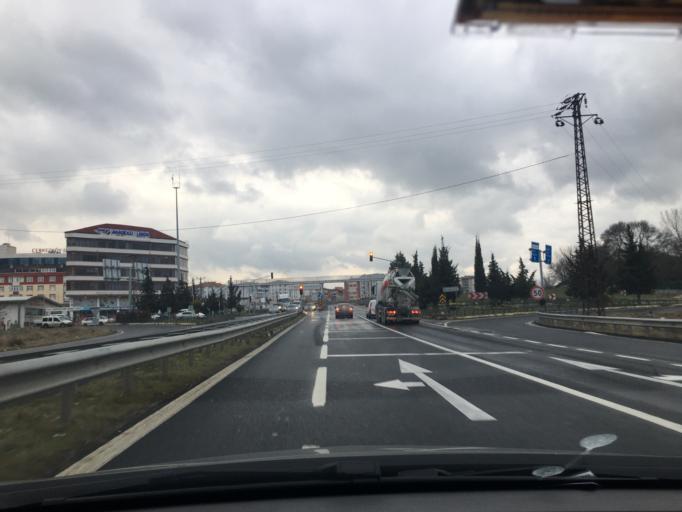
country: TR
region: Tekirdag
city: Cerkezkoey
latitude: 41.2830
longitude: 28.0151
